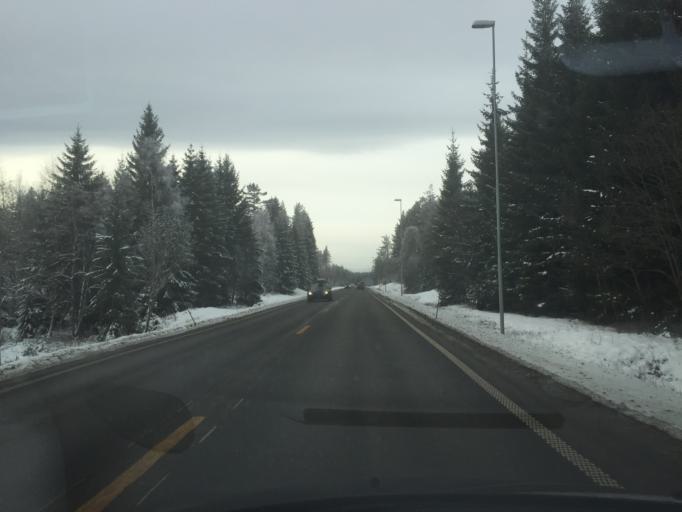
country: NO
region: Hedmark
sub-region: Elverum
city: Elverum
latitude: 60.9174
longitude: 11.6509
